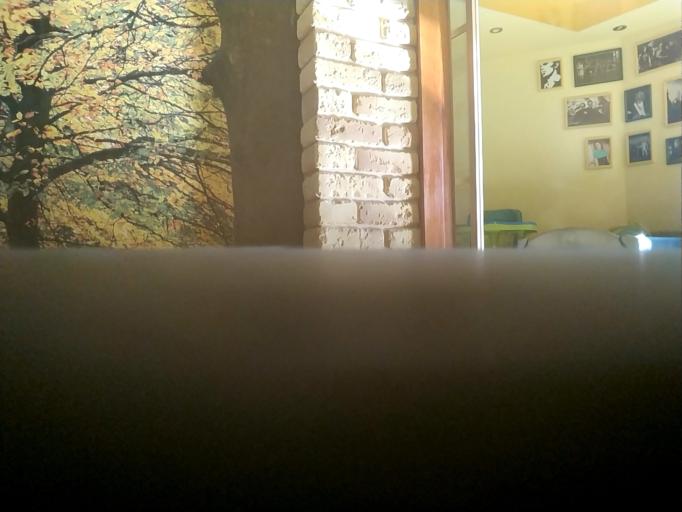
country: RU
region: Smolensk
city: Temkino
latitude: 54.9266
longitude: 34.9656
